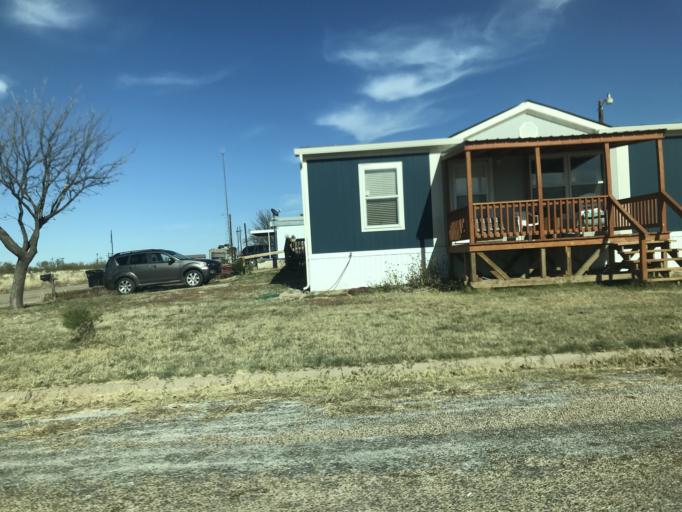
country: US
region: Texas
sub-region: Taylor County
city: Abilene
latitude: 32.5005
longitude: -99.7608
